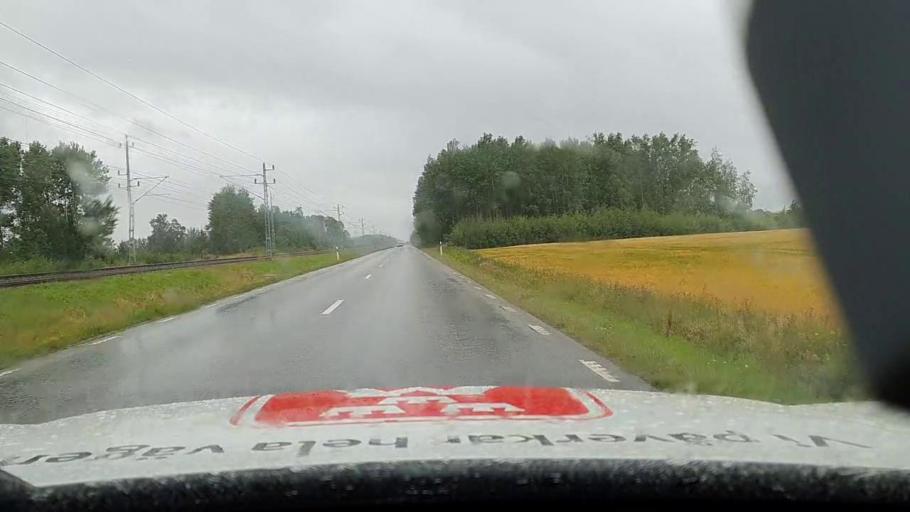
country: SE
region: Vaestra Goetaland
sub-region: Toreboda Kommun
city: Toereboda
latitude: 58.6847
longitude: 14.1088
